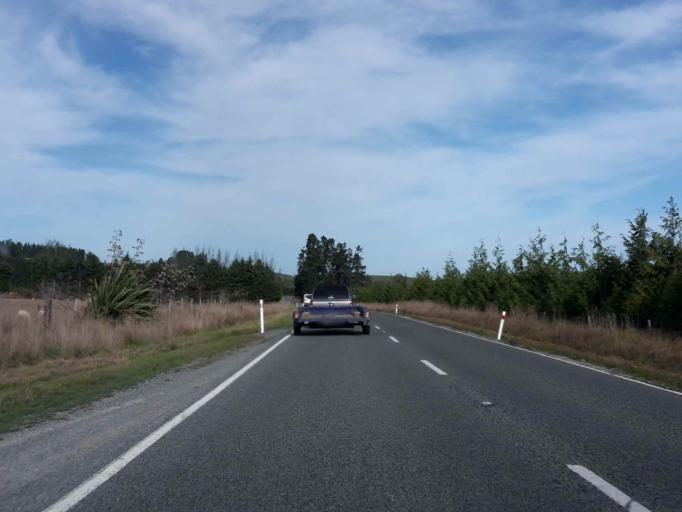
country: NZ
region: Canterbury
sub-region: Timaru District
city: Pleasant Point
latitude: -44.0871
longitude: 170.9868
